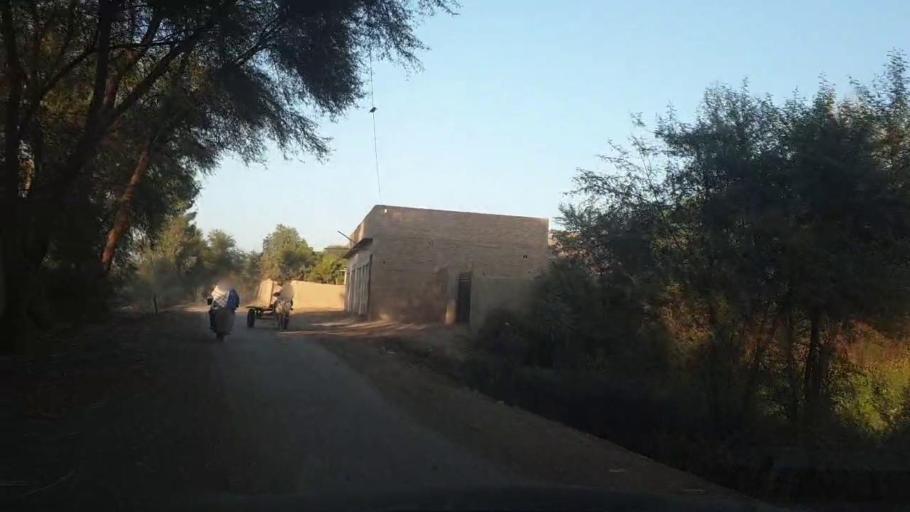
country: PK
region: Sindh
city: Ubauro
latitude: 28.1692
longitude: 69.5824
